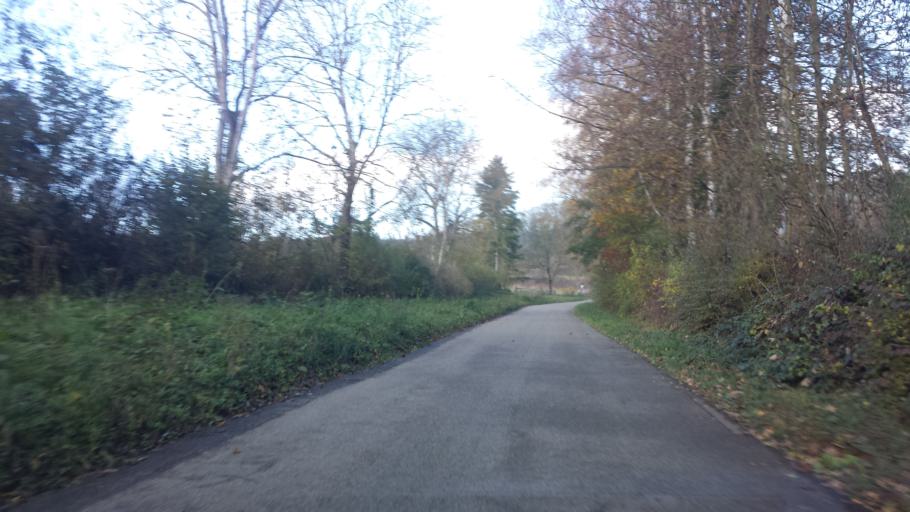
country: DE
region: Baden-Wuerttemberg
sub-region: Karlsruhe Region
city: Ostringen
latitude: 49.1614
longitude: 8.6970
